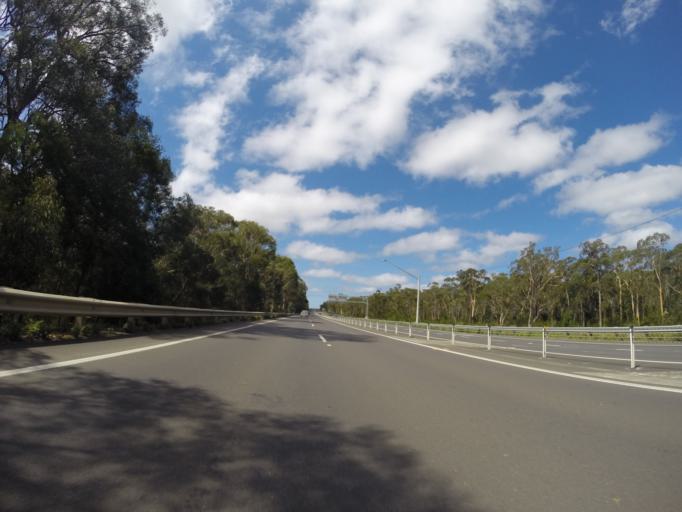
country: AU
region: New South Wales
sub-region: Shoalhaven Shire
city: Falls Creek
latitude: -34.9821
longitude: 150.5882
